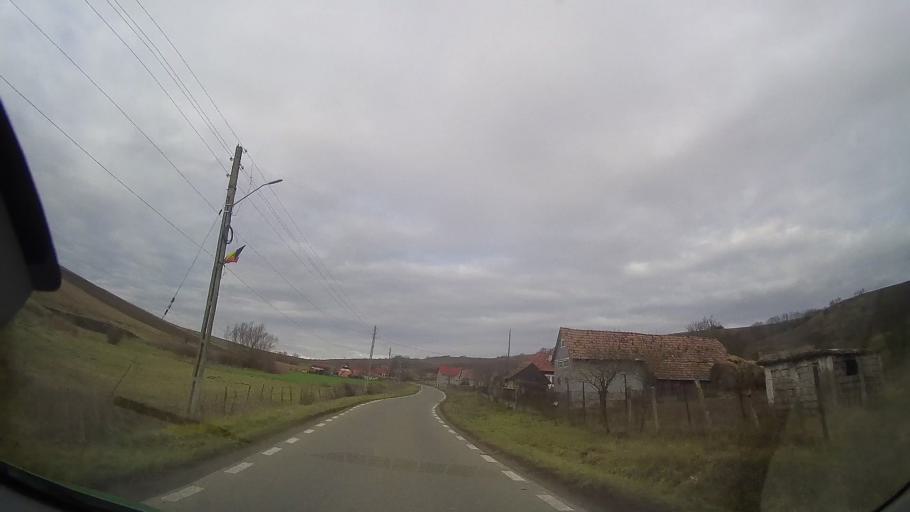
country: RO
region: Mures
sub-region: Comuna Cozma
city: Cozma
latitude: 46.8123
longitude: 24.4993
